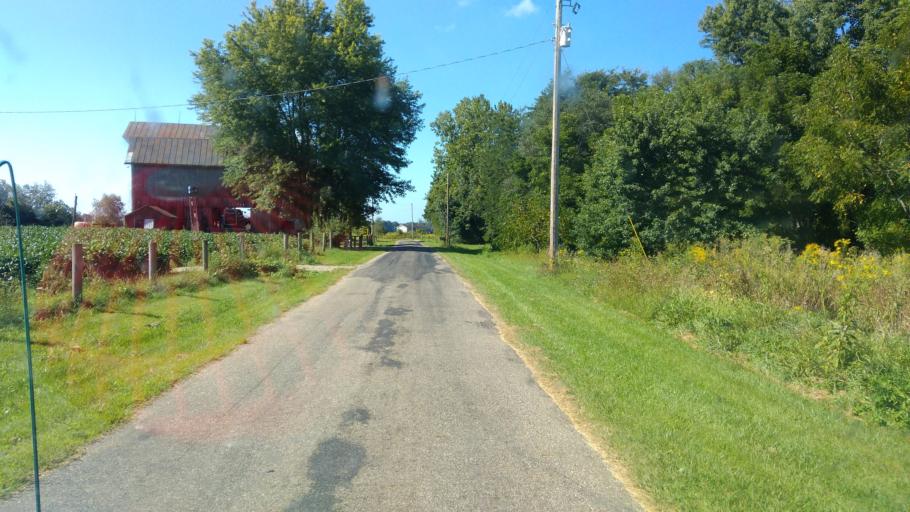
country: US
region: Ohio
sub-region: Knox County
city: Fredericktown
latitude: 40.4477
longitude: -82.4967
